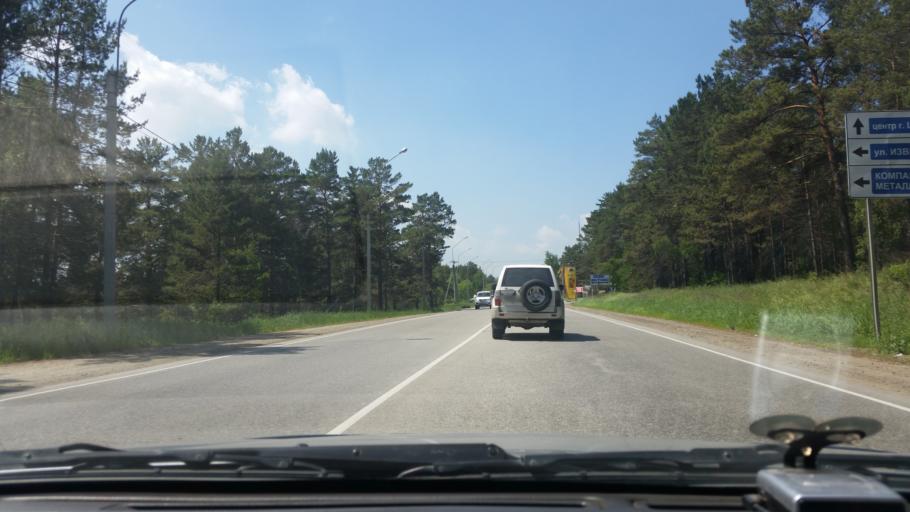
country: RU
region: Irkutsk
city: Shelekhov
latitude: 52.2131
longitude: 104.1152
